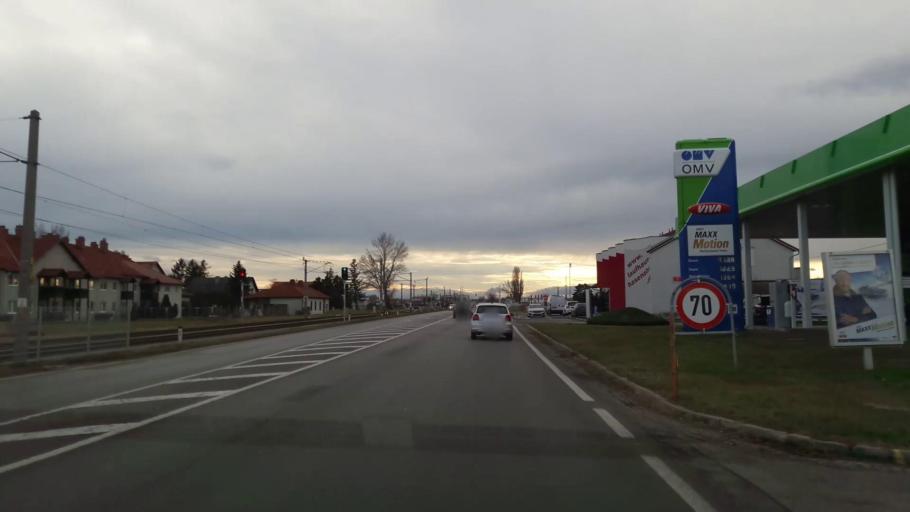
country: AT
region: Lower Austria
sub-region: Politischer Bezirk Modling
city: Guntramsdorf
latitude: 48.0392
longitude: 16.3038
